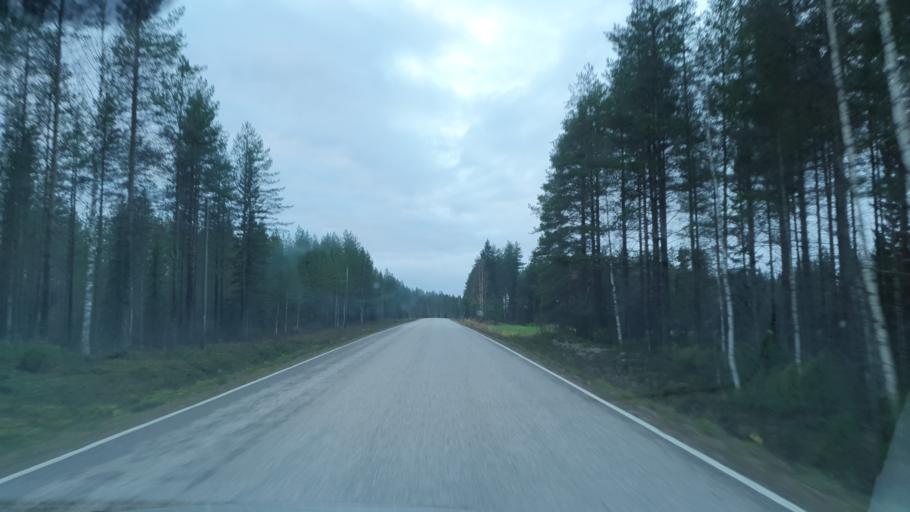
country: FI
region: Kainuu
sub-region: Kajaani
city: Ristijaervi
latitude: 64.4211
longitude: 28.4073
